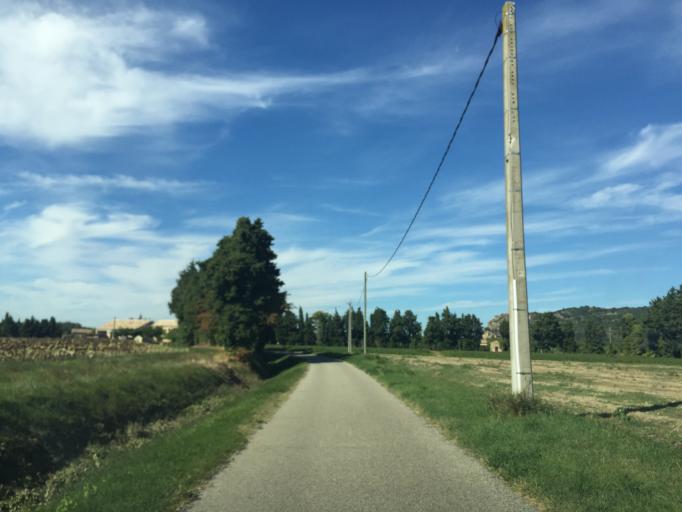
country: FR
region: Provence-Alpes-Cote d'Azur
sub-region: Departement du Vaucluse
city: Mornas
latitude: 44.1885
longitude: 4.7328
